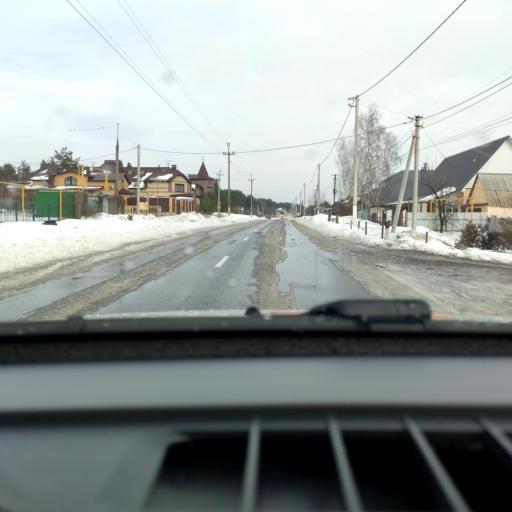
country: RU
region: Voronezj
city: Podgornoye
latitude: 51.7745
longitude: 39.1259
